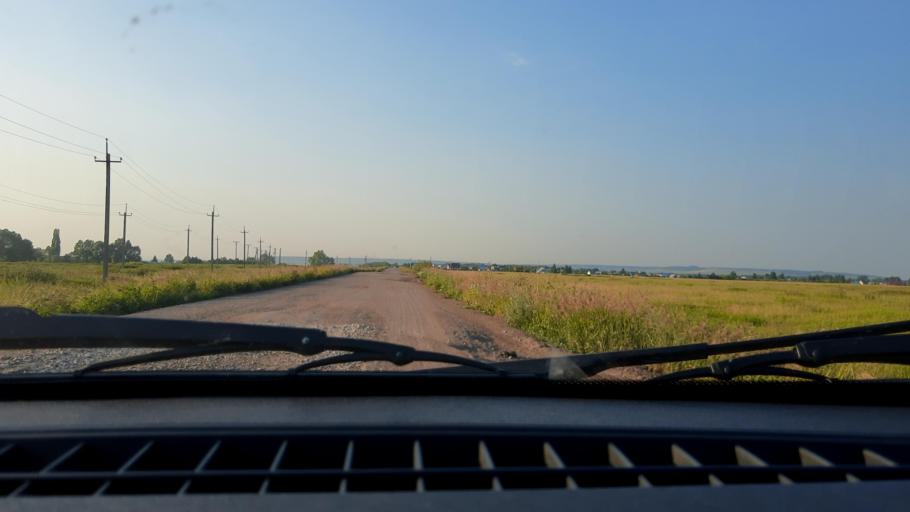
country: RU
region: Bashkortostan
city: Asanovo
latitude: 54.9088
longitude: 55.6267
